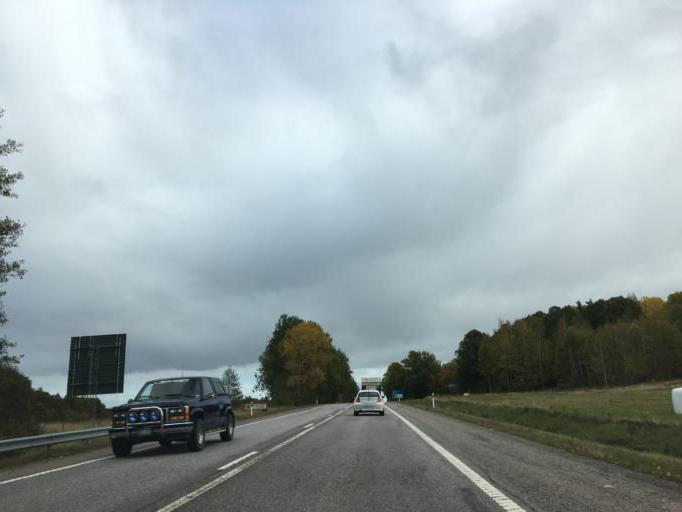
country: SE
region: Soedermanland
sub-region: Nykopings Kommun
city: Nykoping
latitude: 58.7691
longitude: 16.9570
